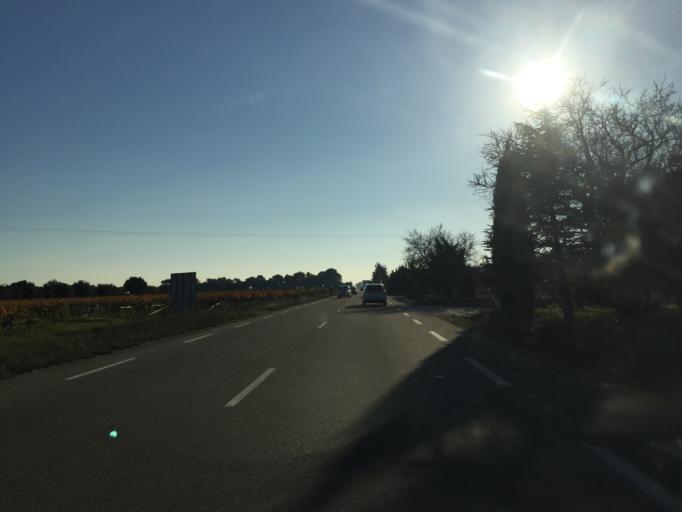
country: FR
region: Provence-Alpes-Cote d'Azur
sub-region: Departement du Vaucluse
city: Sainte-Cecile-les-Vignes
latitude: 44.2296
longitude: 4.8803
